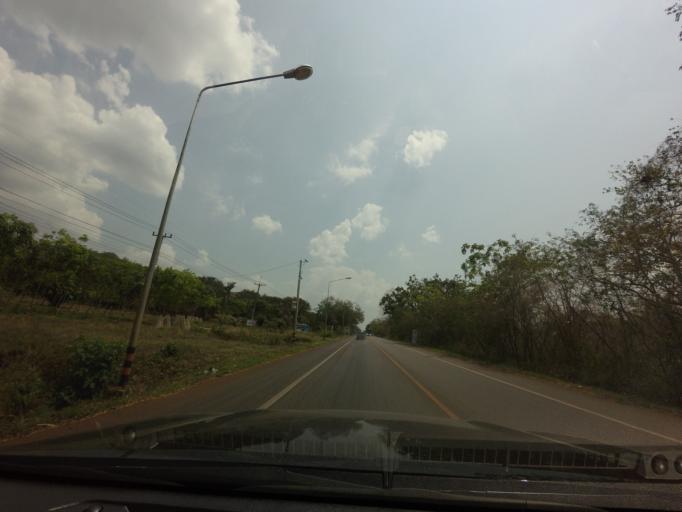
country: TH
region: Kanchanaburi
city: Sai Yok
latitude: 14.1335
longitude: 99.1572
